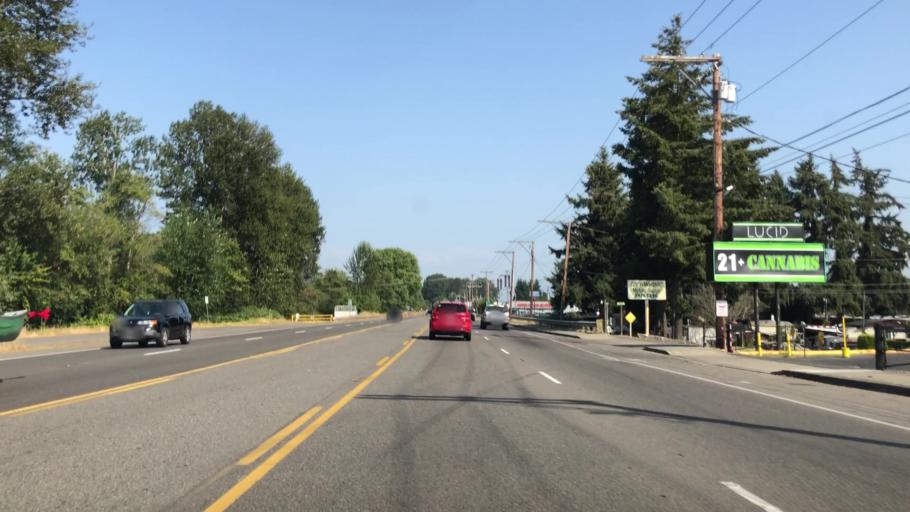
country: US
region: Washington
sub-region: Pierce County
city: Puyallup
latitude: 47.2072
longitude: -122.3234
